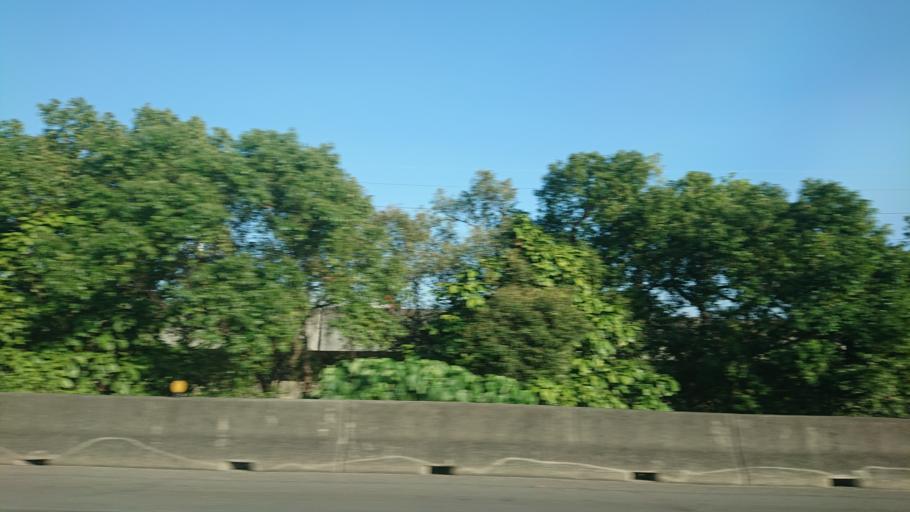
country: TW
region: Taiwan
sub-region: Taichung City
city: Taichung
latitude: 24.1323
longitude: 120.6175
